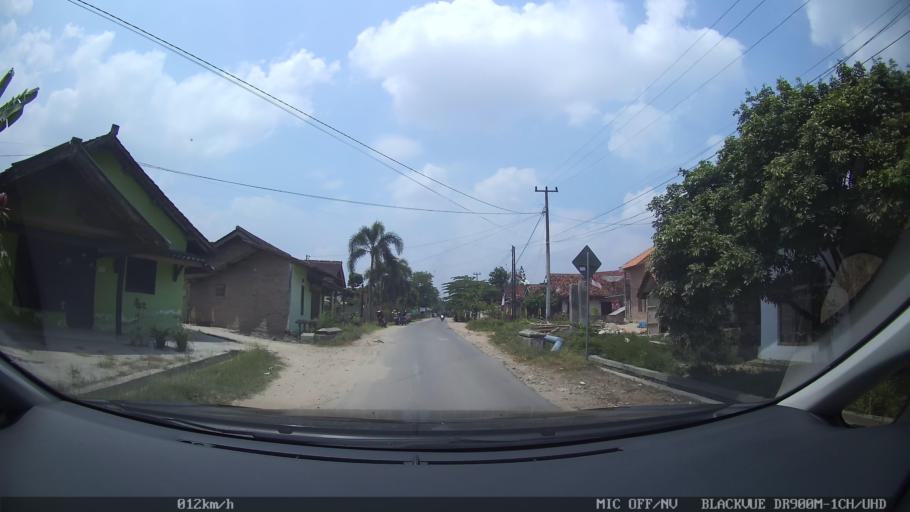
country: ID
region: Lampung
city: Pringsewu
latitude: -5.3460
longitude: 104.9862
